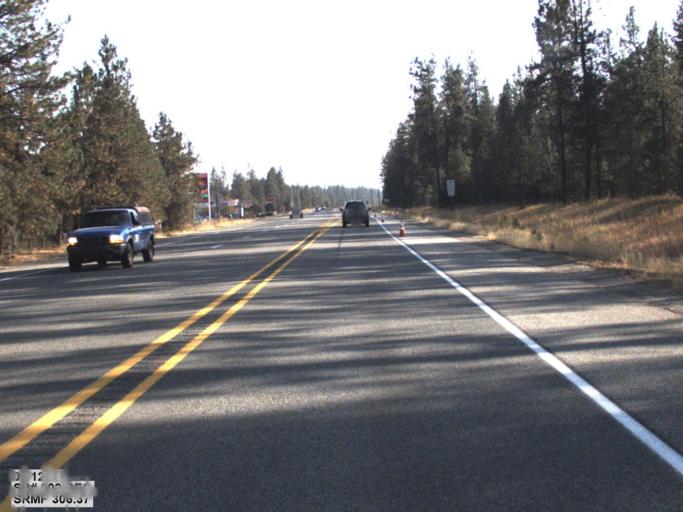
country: US
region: Washington
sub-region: Spokane County
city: Deer Park
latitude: 47.9166
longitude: -117.3501
